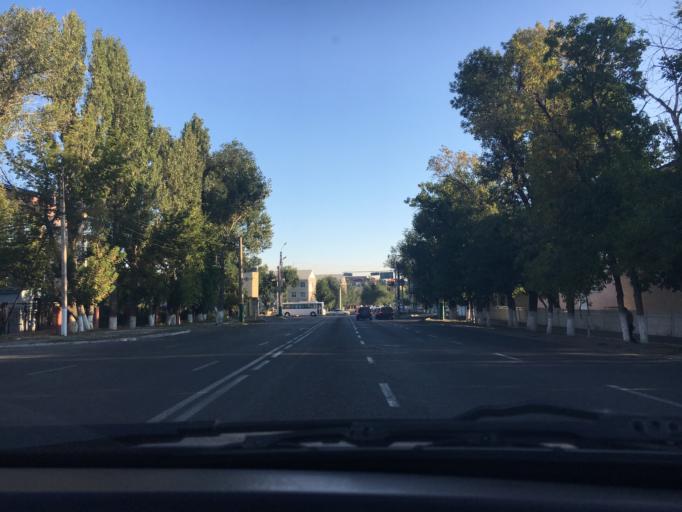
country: KZ
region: Zhambyl
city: Taraz
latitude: 42.8994
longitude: 71.3601
